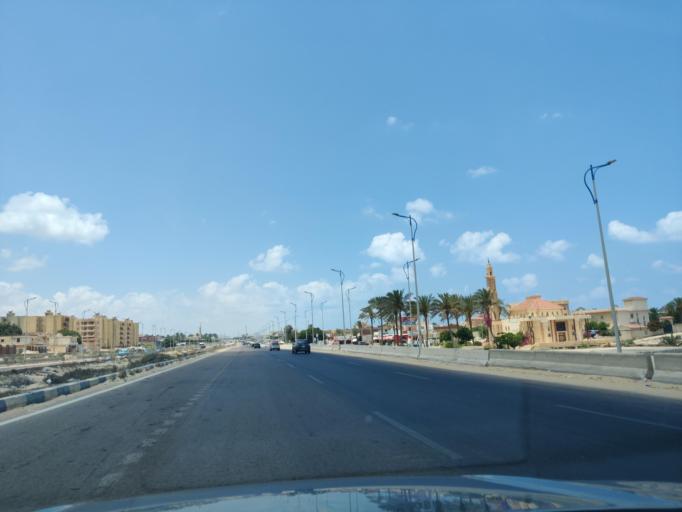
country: EG
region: Alexandria
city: Alexandria
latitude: 30.9908
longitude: 29.5953
